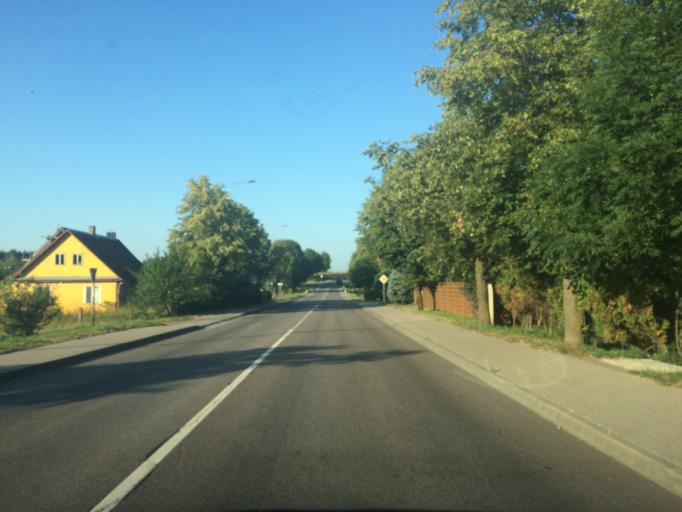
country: LT
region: Vilnius County
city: Ukmerge
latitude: 55.3041
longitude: 24.8617
